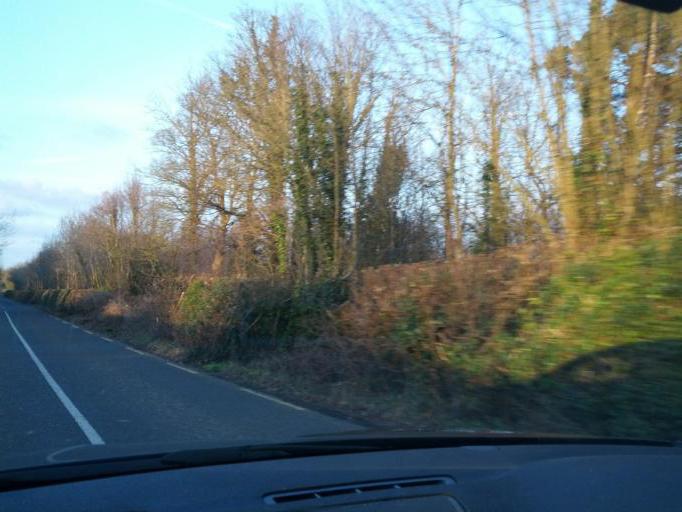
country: IE
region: Munster
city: Nenagh Bridge
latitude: 52.9390
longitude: -8.2419
